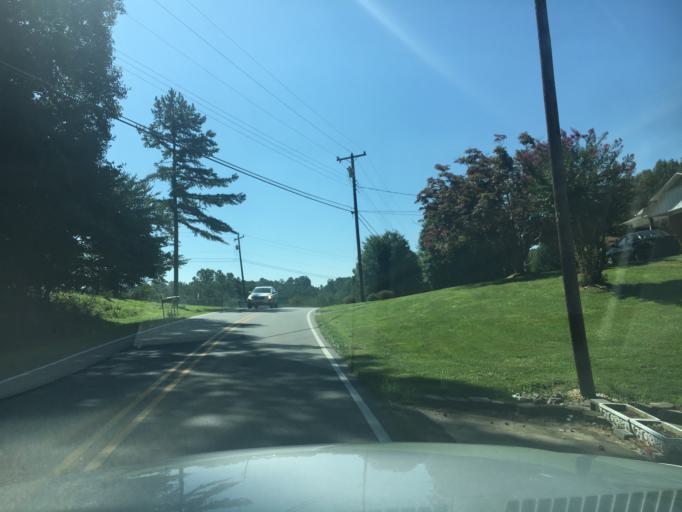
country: US
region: North Carolina
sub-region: McDowell County
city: West Marion
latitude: 35.6639
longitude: -82.0357
